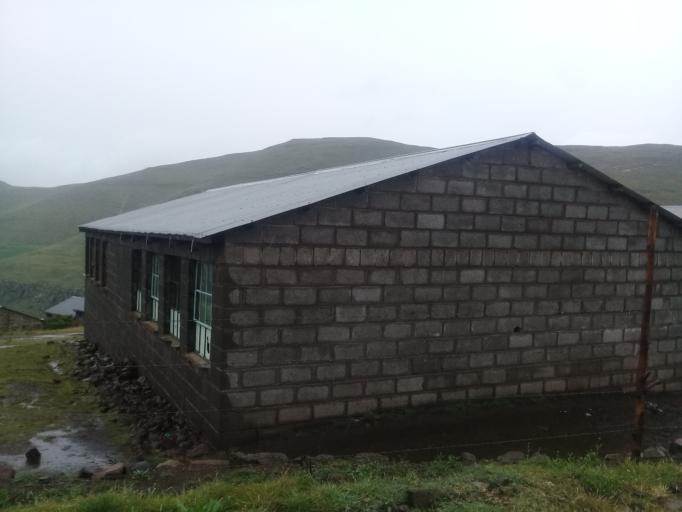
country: LS
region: Mokhotlong
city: Mokhotlong
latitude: -29.3875
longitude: 28.9499
